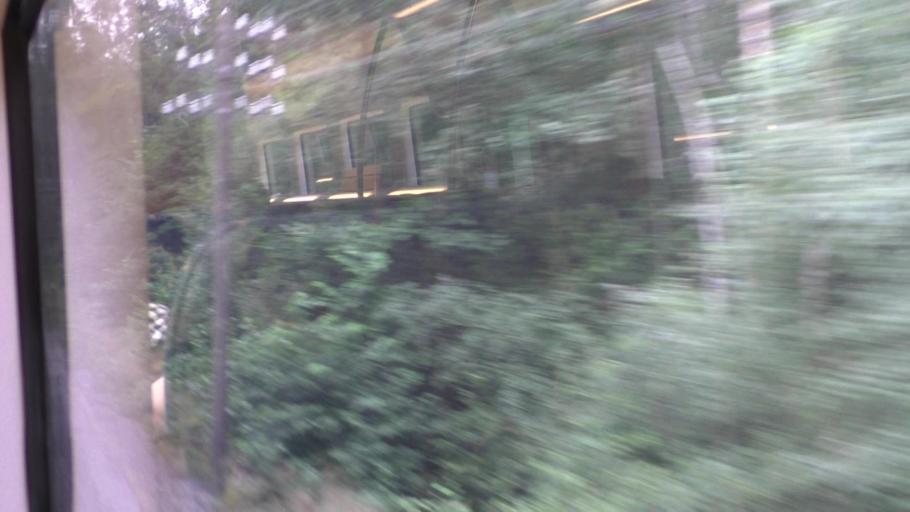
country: DE
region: Saxony
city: Horka
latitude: 51.2730
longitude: 14.9062
